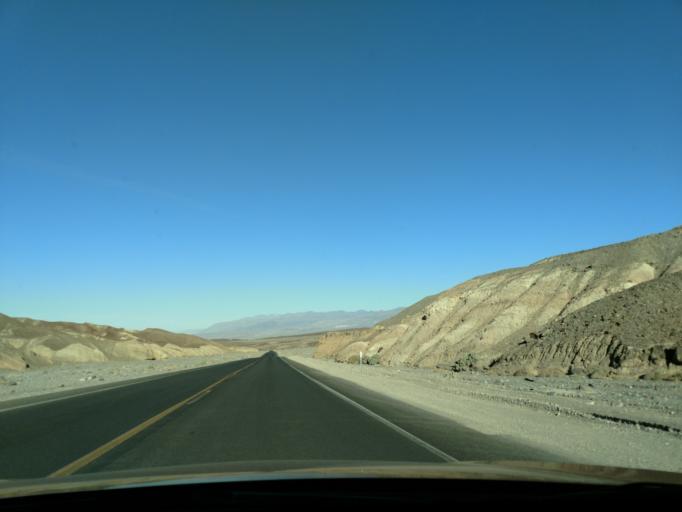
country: US
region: Nevada
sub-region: Nye County
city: Beatty
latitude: 36.4219
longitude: -116.8095
